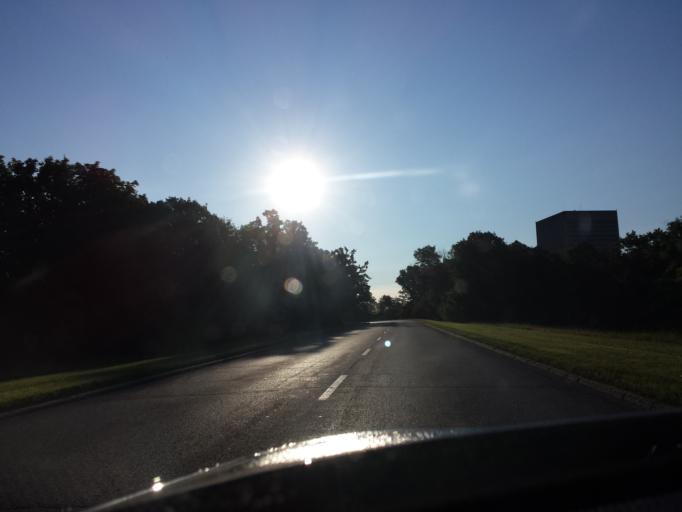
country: CA
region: Ontario
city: Ottawa
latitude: 45.4068
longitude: -75.7453
